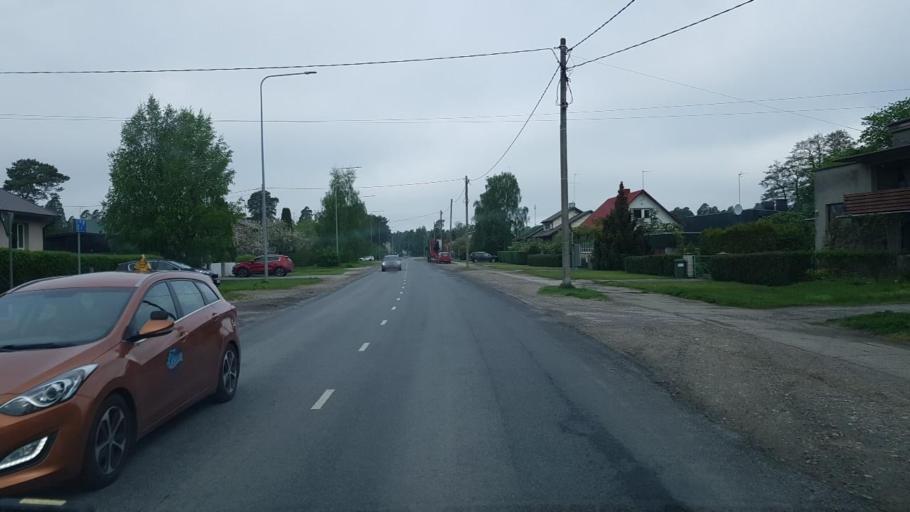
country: EE
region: Laeaene
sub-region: Haapsalu linn
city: Haapsalu
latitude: 58.9296
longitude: 23.5323
